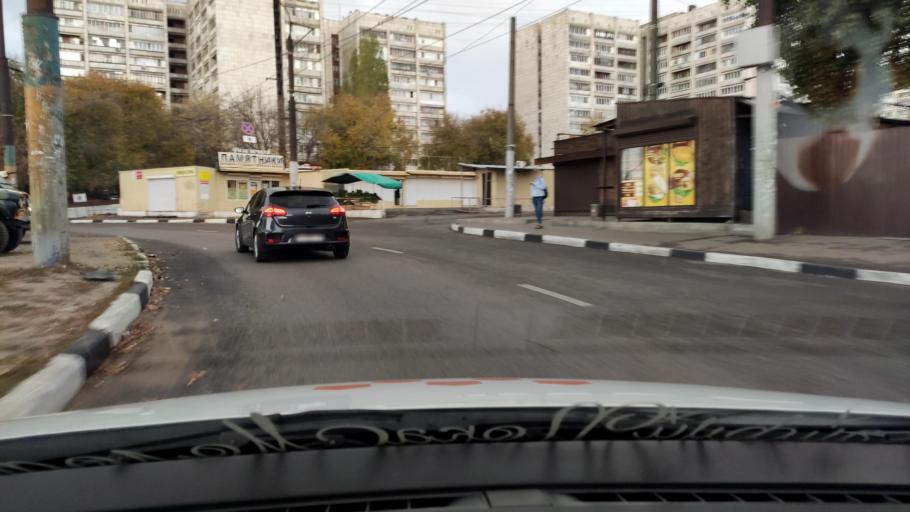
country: RU
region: Voronezj
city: Podgornoye
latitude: 51.7023
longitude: 39.1635
